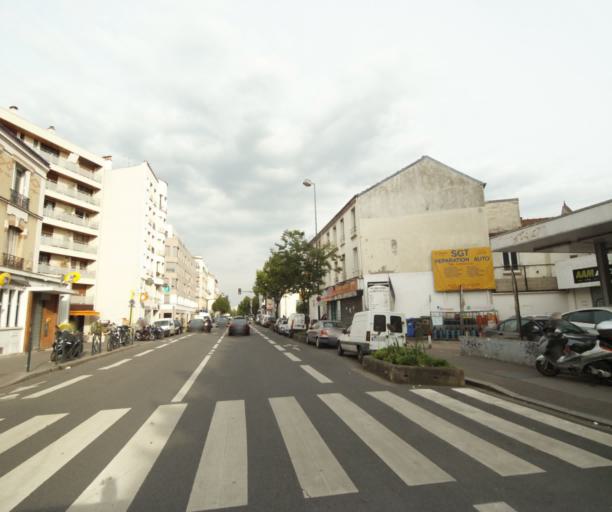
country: FR
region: Ile-de-France
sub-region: Paris
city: Saint-Ouen
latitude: 48.8964
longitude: 2.3360
